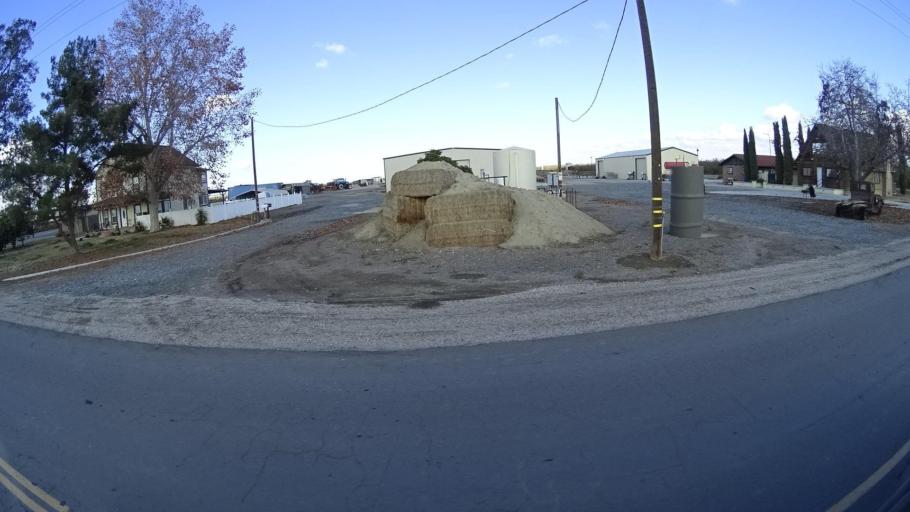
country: US
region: California
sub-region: Kern County
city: McFarland
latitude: 35.6887
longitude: -119.2684
